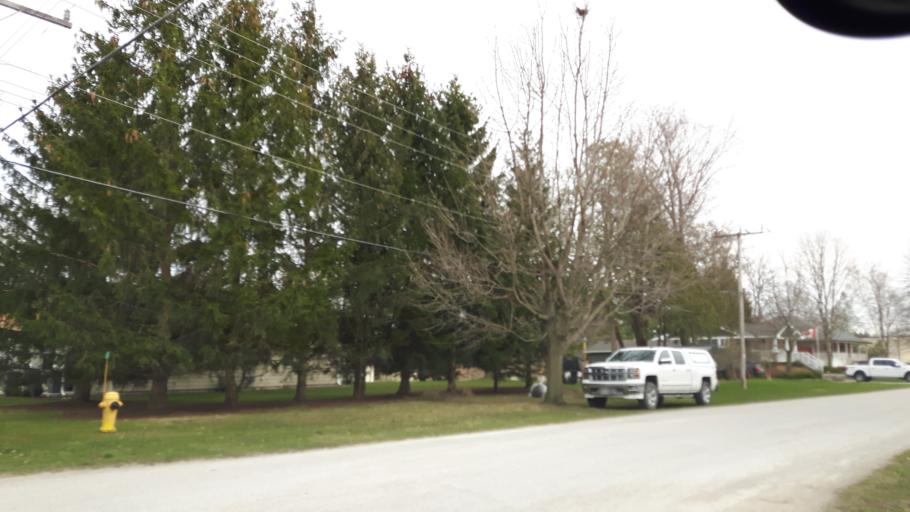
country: CA
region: Ontario
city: Bluewater
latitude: 43.5618
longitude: -81.6980
